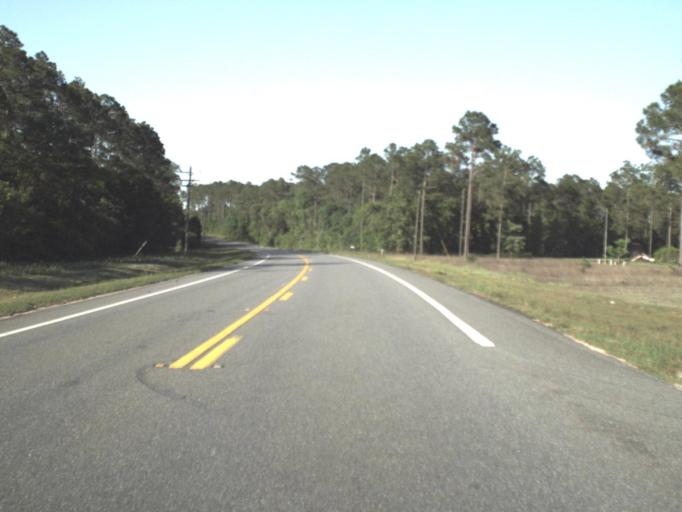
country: US
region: Florida
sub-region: Liberty County
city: Bristol
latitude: 30.4193
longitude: -84.7808
